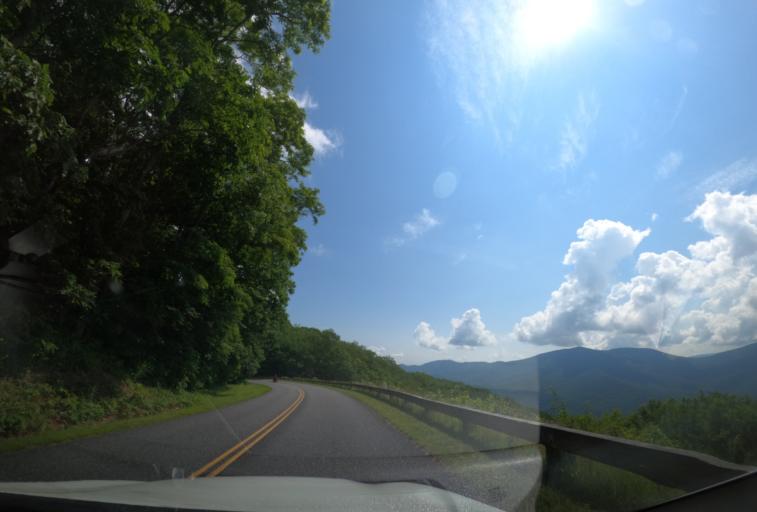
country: US
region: North Carolina
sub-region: Haywood County
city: Hazelwood
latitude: 35.4261
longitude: -83.0348
